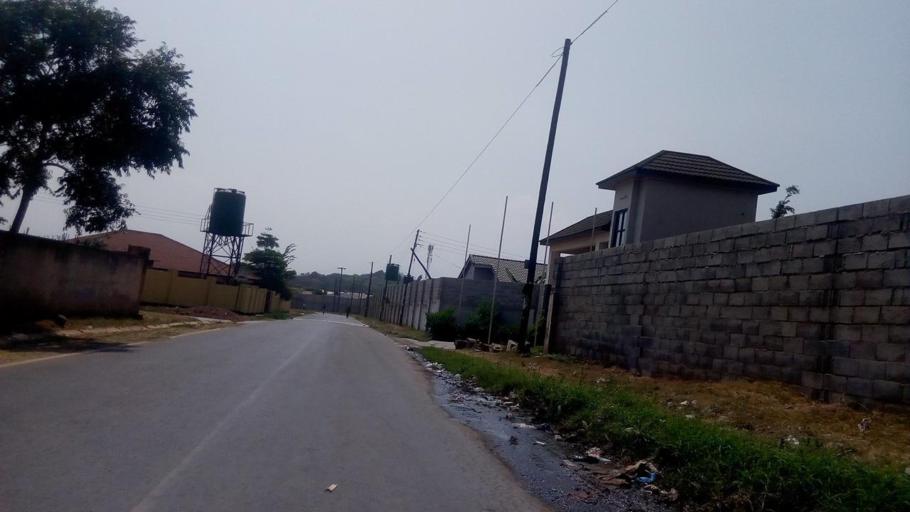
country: ZM
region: Lusaka
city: Lusaka
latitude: -15.3624
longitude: 28.2847
